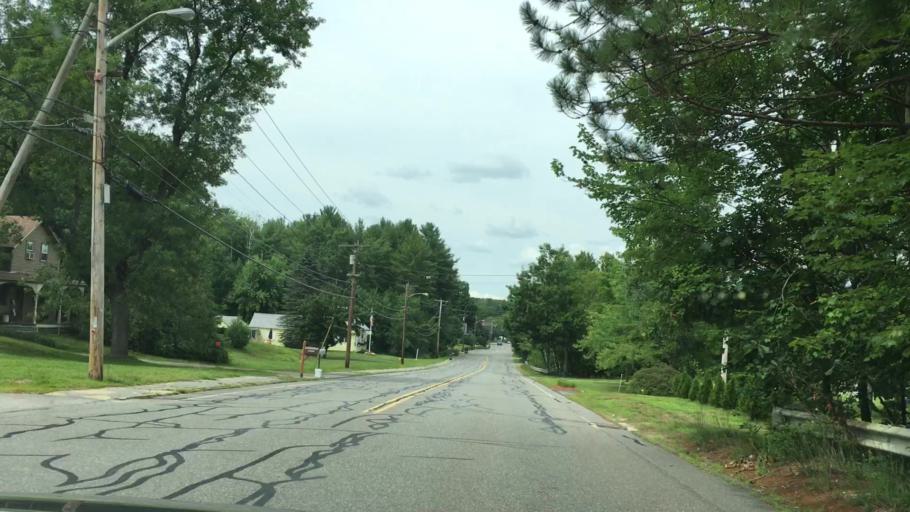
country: US
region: Massachusetts
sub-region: Worcester County
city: Winchendon
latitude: 42.6896
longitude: -72.0154
